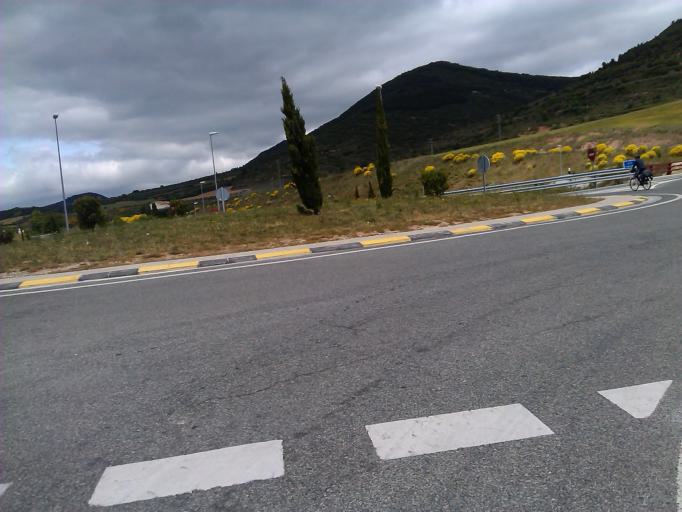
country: ES
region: Navarre
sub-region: Provincia de Navarra
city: Cirauqui
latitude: 42.6754
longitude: -1.8835
